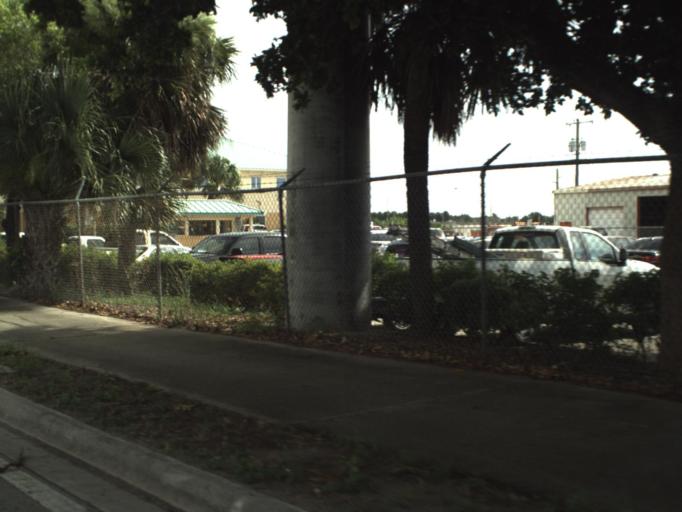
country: US
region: Florida
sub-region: Palm Beach County
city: Delray Beach
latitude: 26.4331
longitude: -80.0922
